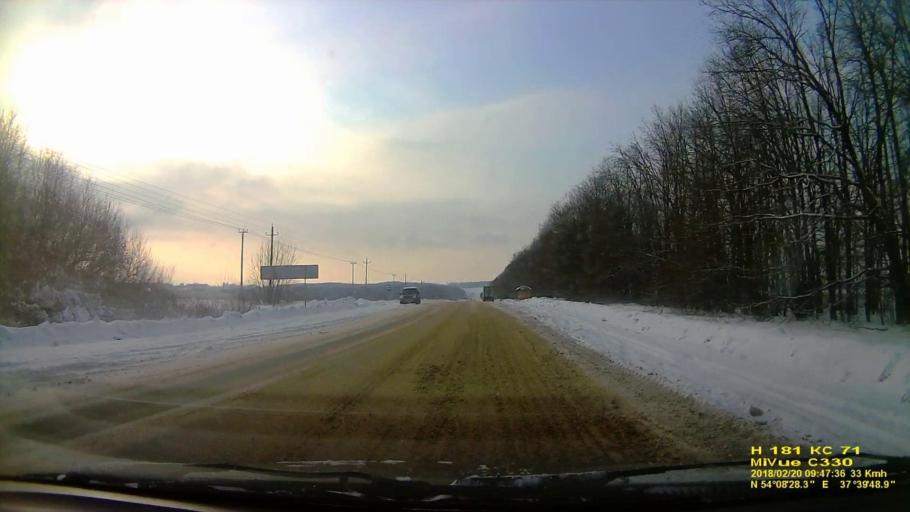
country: RU
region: Tula
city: Tula
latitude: 54.1413
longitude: 37.6635
